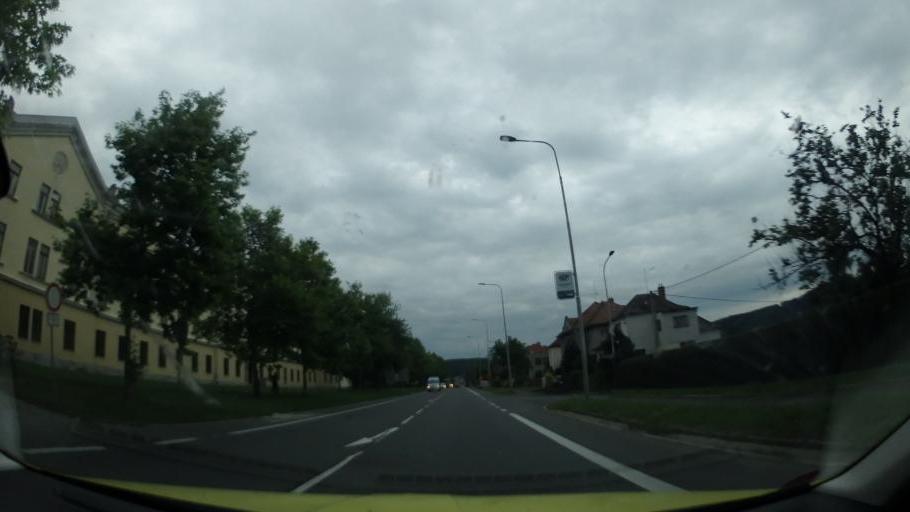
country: CZ
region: Olomoucky
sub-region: Okres Prerov
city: Hranice
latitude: 49.5514
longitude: 17.7189
